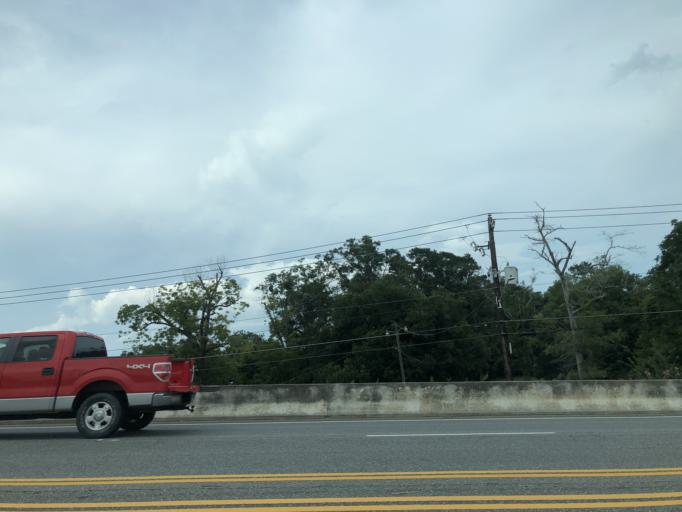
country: US
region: Georgia
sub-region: Wayne County
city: Jesup
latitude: 31.6062
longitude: -81.8795
